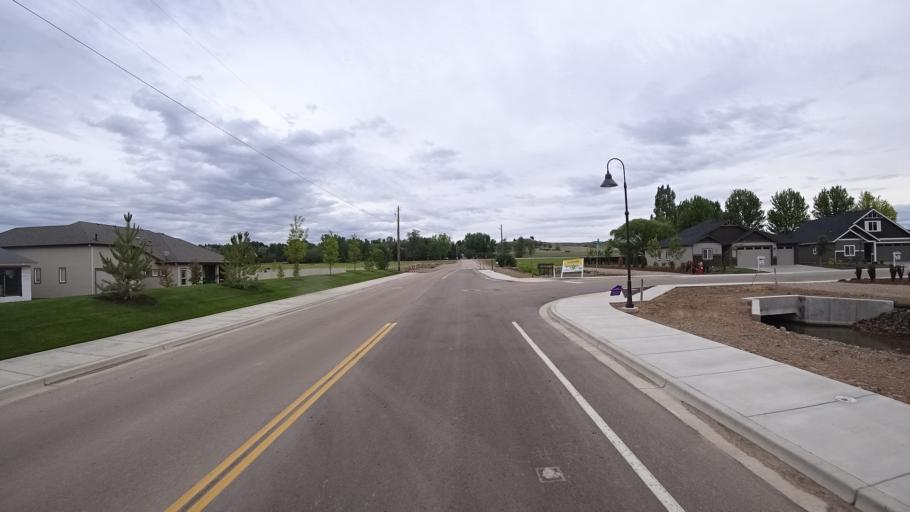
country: US
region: Idaho
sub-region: Ada County
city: Star
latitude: 43.7154
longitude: -116.5032
